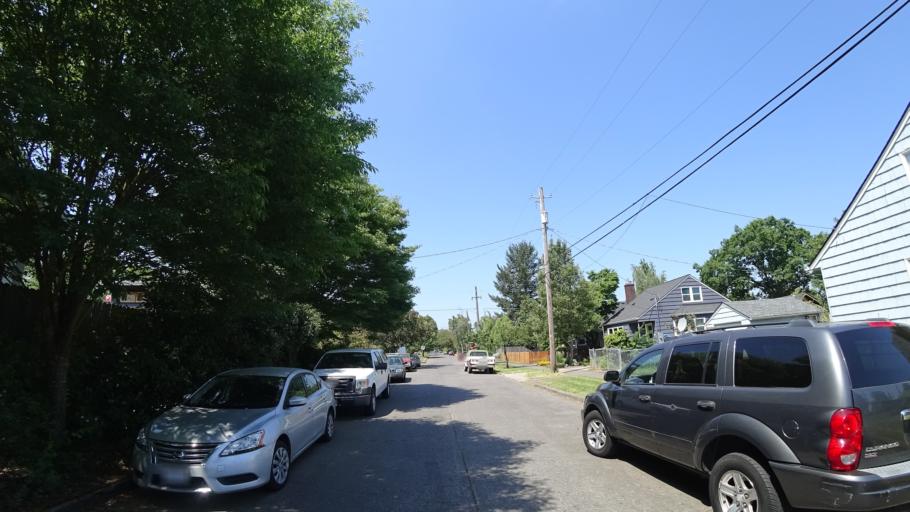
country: US
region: Oregon
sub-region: Multnomah County
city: Portland
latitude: 45.5646
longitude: -122.6504
